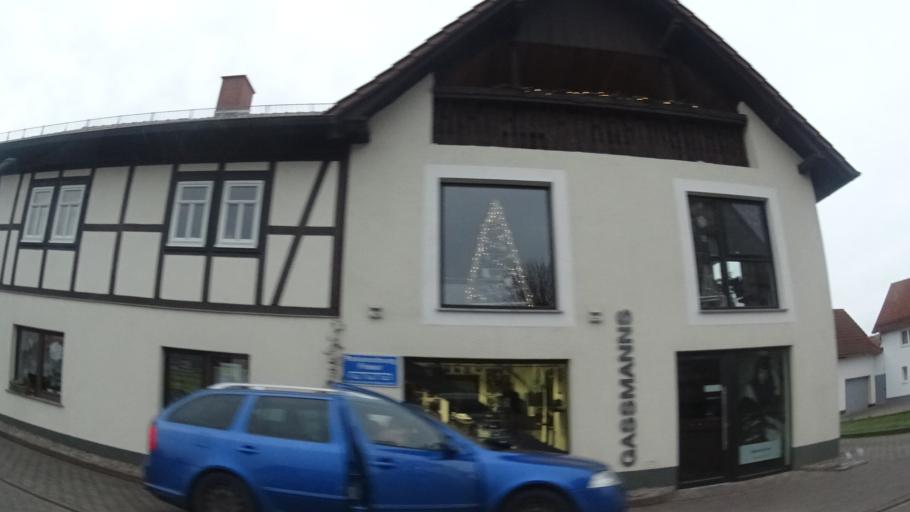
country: DE
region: Thuringia
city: Buttlar
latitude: 50.7569
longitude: 9.9532
